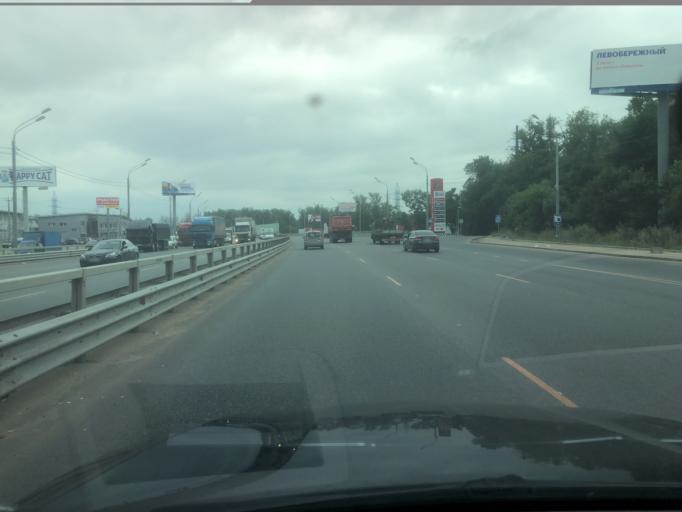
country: RU
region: Moscow
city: Severnyy
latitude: 55.9630
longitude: 37.5332
